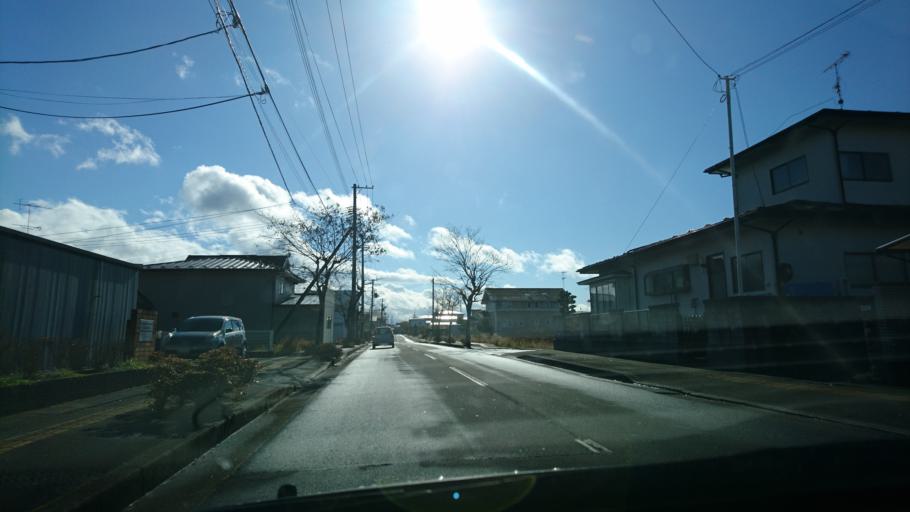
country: JP
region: Iwate
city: Ichinoseki
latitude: 38.9435
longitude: 141.1313
